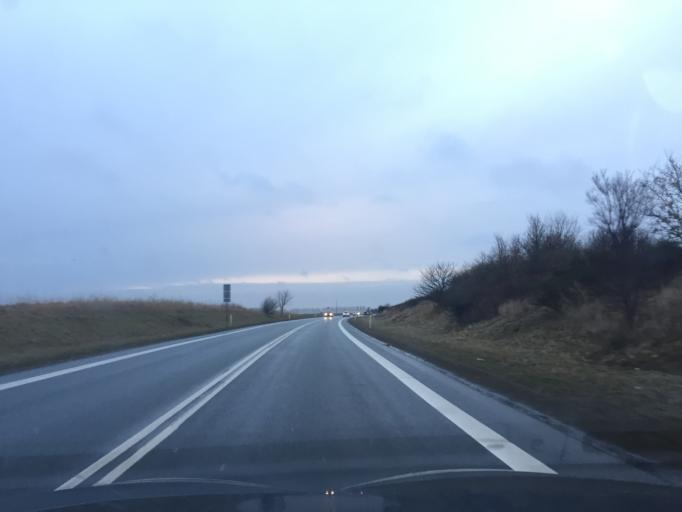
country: DK
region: Zealand
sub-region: Slagelse Kommune
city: Slagelse
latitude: 55.3685
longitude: 11.3286
